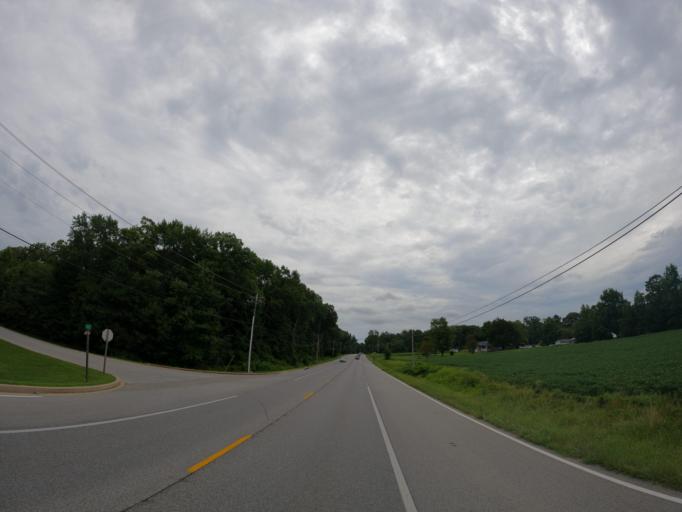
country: US
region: Maryland
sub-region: Saint Mary's County
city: California
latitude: 38.2387
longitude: -76.5402
